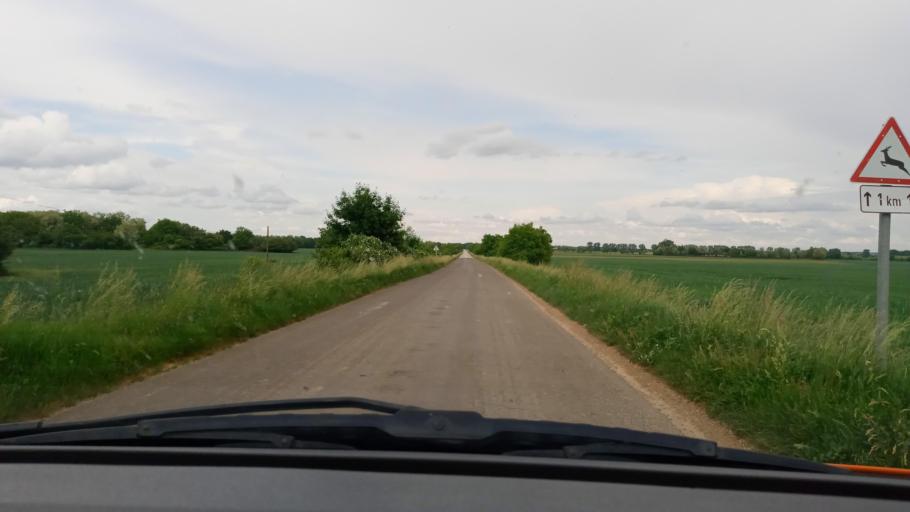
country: HU
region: Baranya
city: Harkany
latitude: 45.9113
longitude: 18.1406
